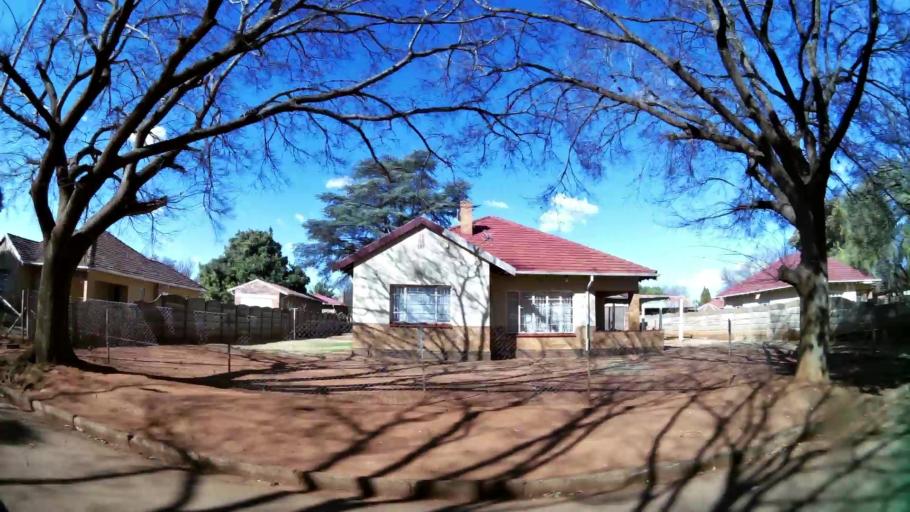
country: ZA
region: Gauteng
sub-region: West Rand District Municipality
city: Carletonville
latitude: -26.3612
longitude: 27.3967
